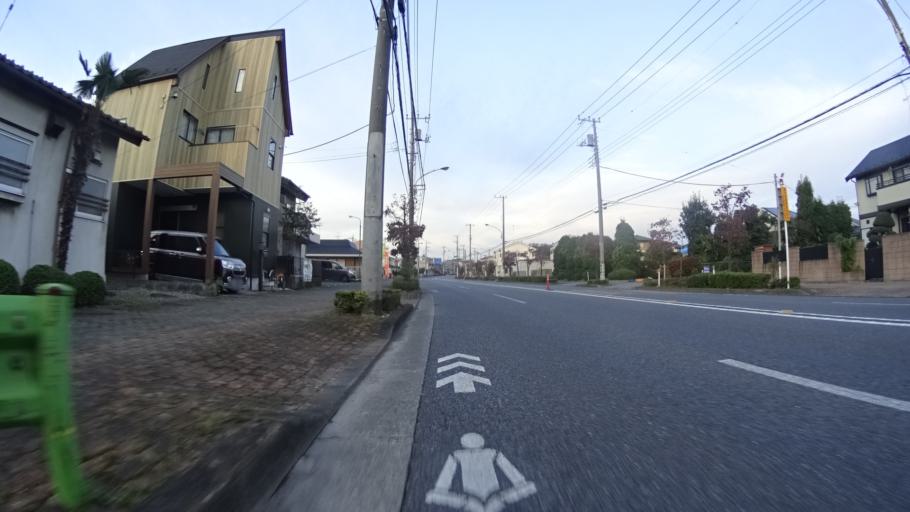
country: JP
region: Tokyo
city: Fussa
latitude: 35.7203
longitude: 139.3203
